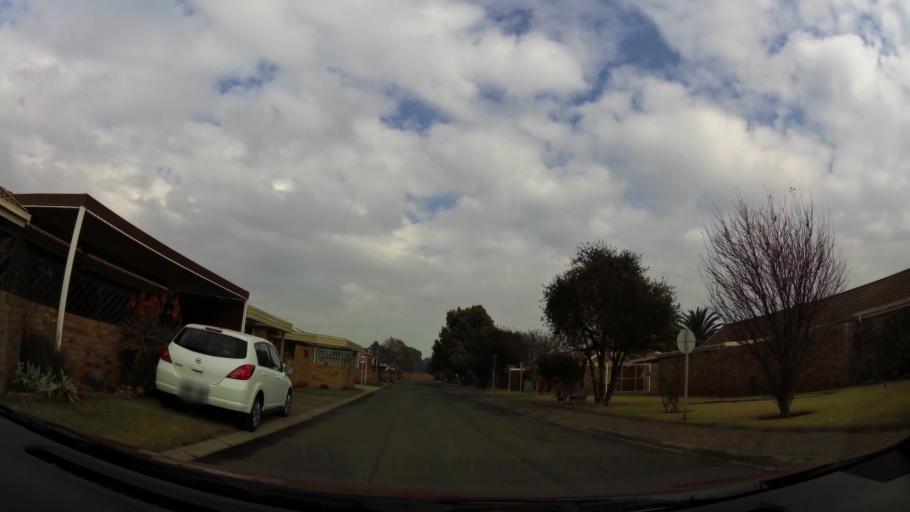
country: ZA
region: Gauteng
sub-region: Sedibeng District Municipality
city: Vanderbijlpark
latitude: -26.7062
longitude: 27.8264
